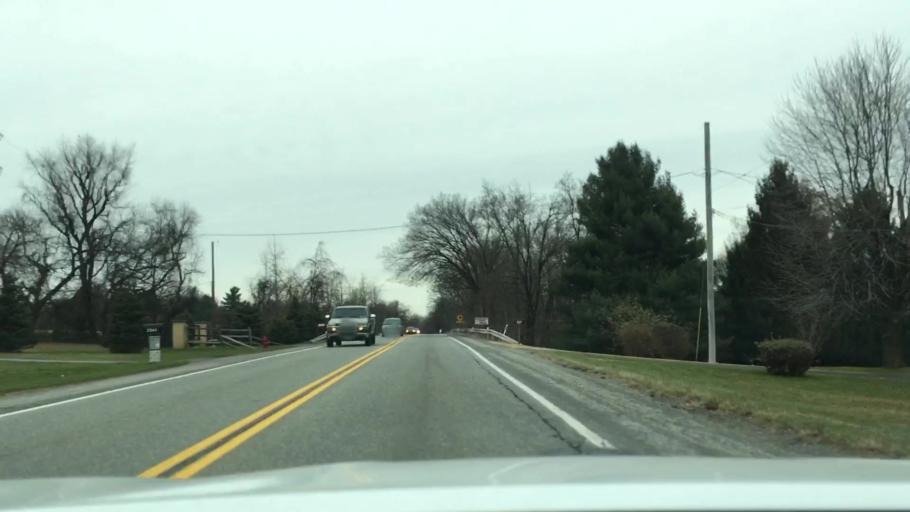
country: US
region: Pennsylvania
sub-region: Montgomery County
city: Sanatoga
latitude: 40.2113
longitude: -75.5979
